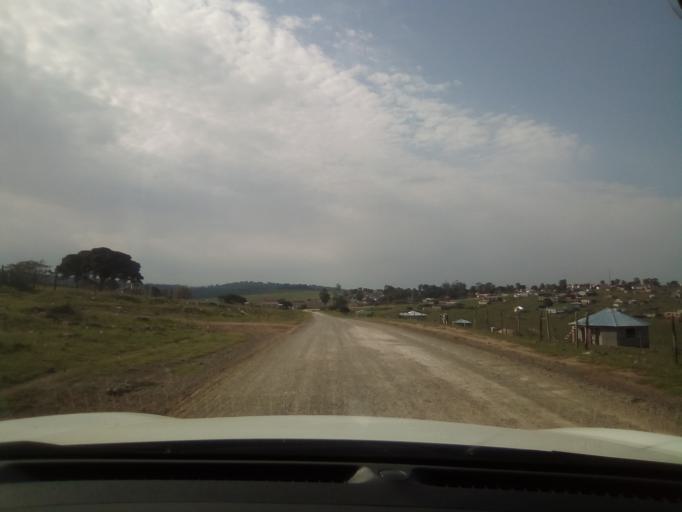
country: ZA
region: Eastern Cape
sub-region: Buffalo City Metropolitan Municipality
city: Bhisho
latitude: -32.9864
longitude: 27.2592
